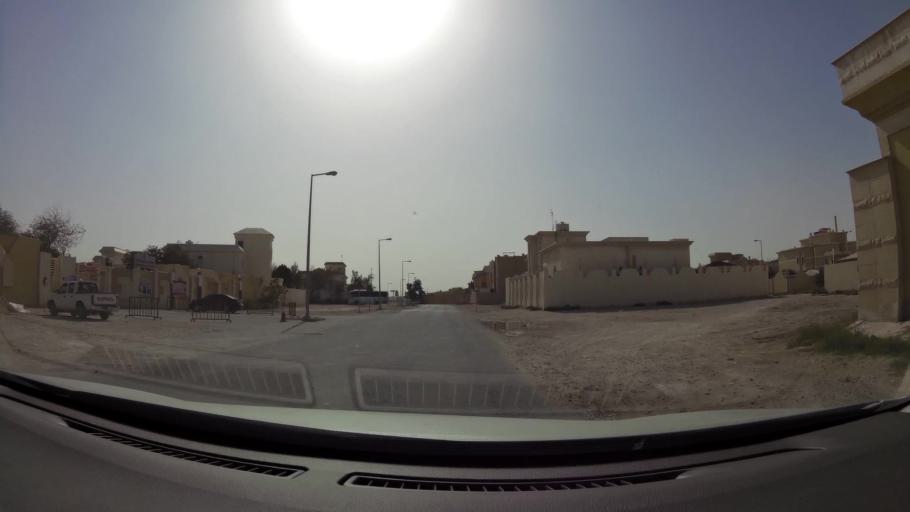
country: QA
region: Baladiyat ar Rayyan
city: Ar Rayyan
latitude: 25.3517
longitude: 51.4445
